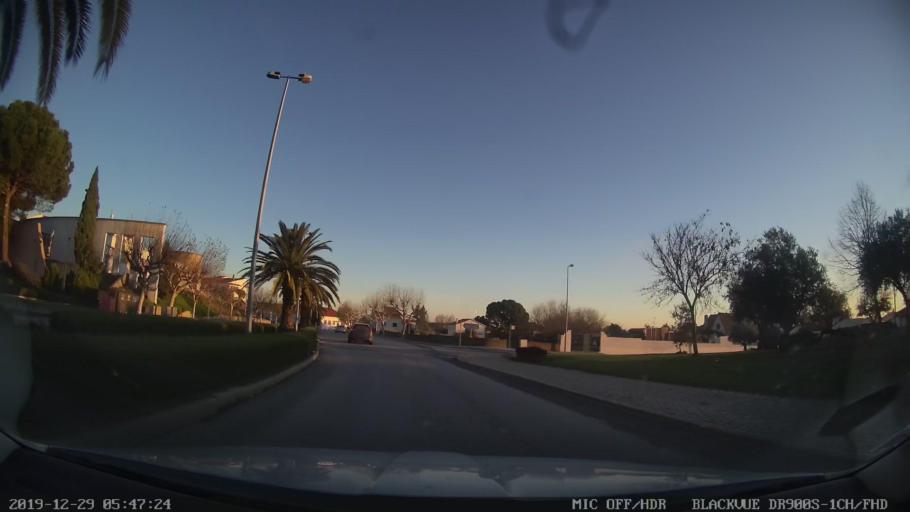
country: PT
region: Castelo Branco
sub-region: Idanha-A-Nova
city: Idanha-a-Nova
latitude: 39.9245
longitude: -7.2437
